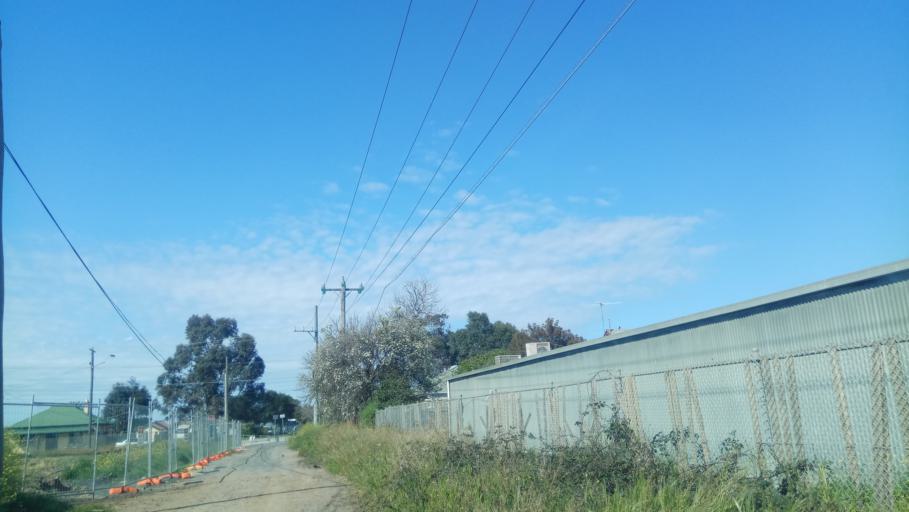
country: AU
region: Victoria
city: Heatherton
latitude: -37.9574
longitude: 145.1182
